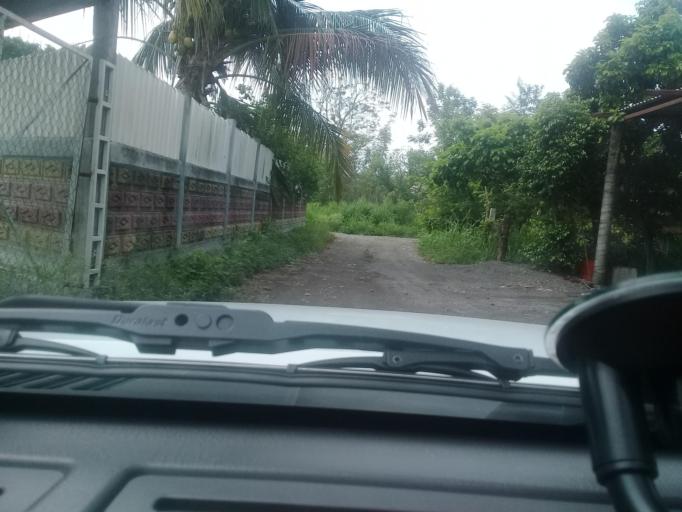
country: MX
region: Veracruz
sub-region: Paso de Ovejas
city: Tolome
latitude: 19.2698
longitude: -96.4004
